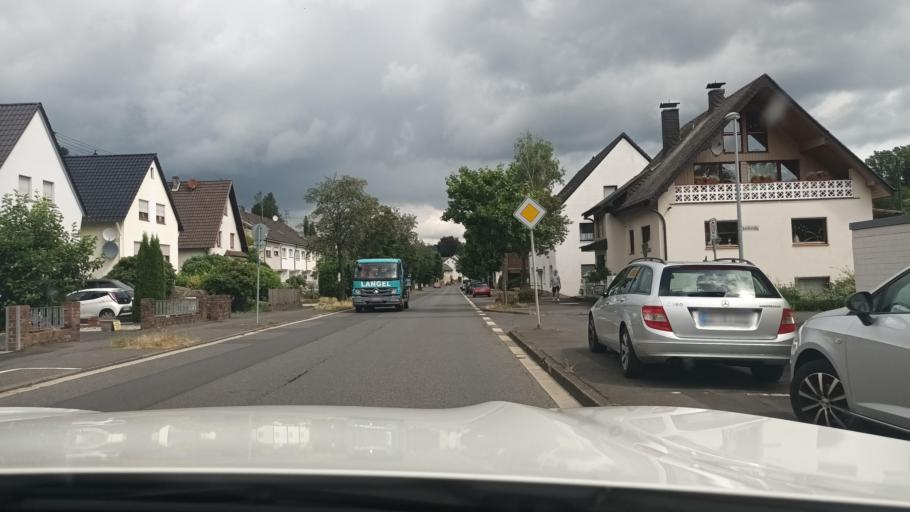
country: DE
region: North Rhine-Westphalia
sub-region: Regierungsbezirk Koln
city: Eitorf
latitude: 50.7623
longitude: 7.4454
